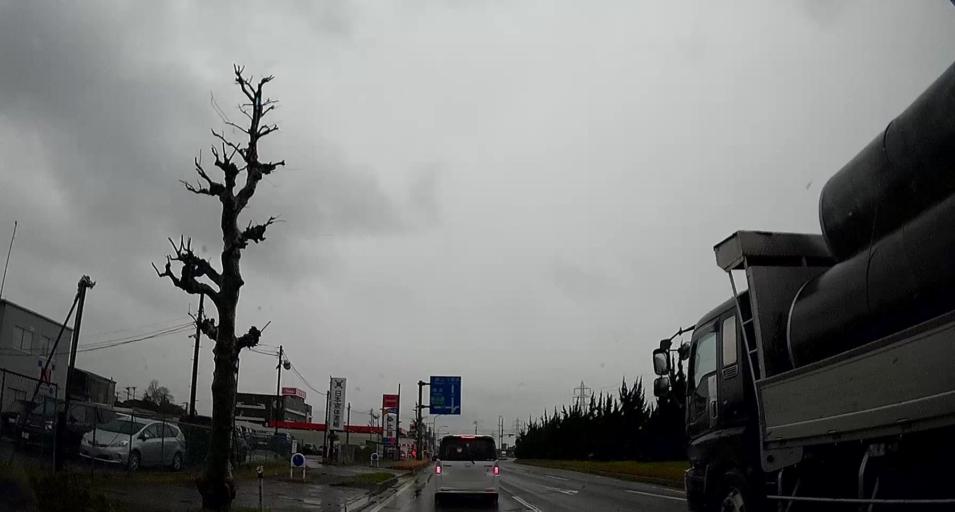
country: JP
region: Chiba
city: Ichihara
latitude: 35.5208
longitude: 140.0623
